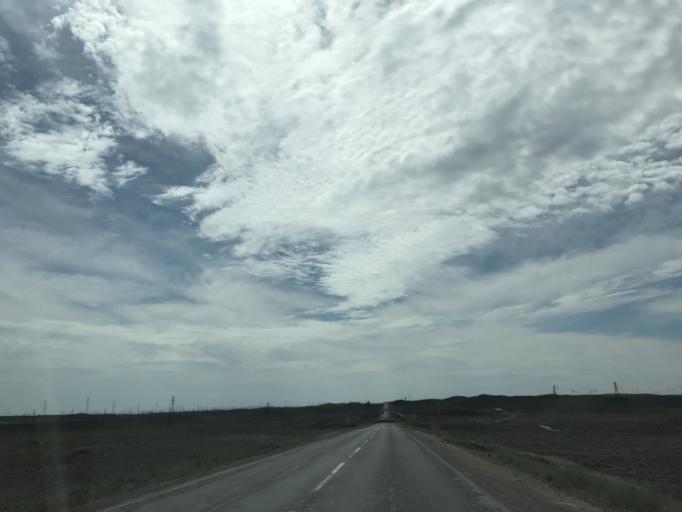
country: KZ
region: Almaty Oblysy
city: Ulken
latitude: 45.2113
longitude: 73.8756
